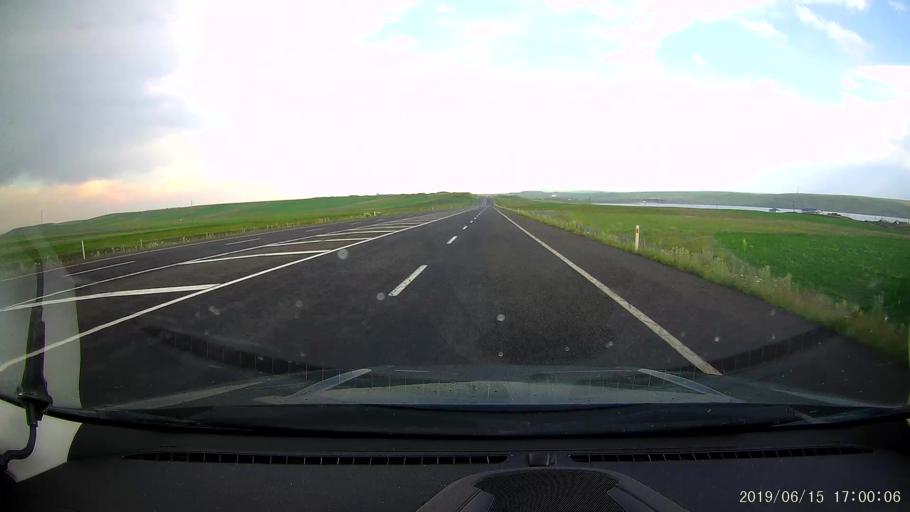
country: TR
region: Kars
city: Susuz
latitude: 40.7431
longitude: 43.1579
